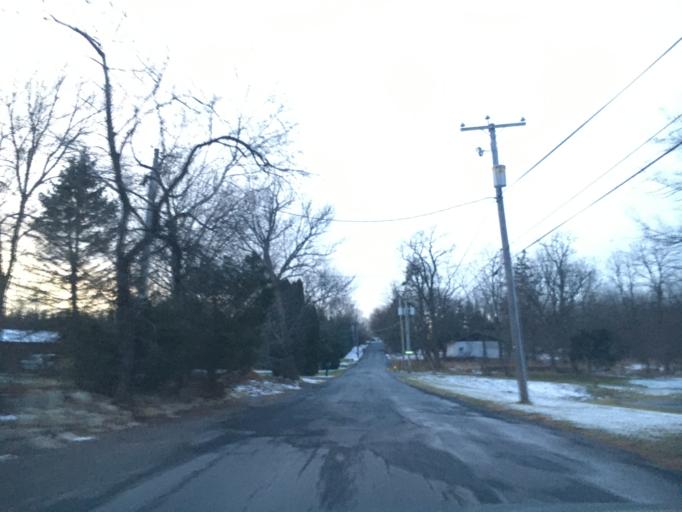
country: US
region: Pennsylvania
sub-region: Northampton County
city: Bath
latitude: 40.7830
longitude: -75.3691
